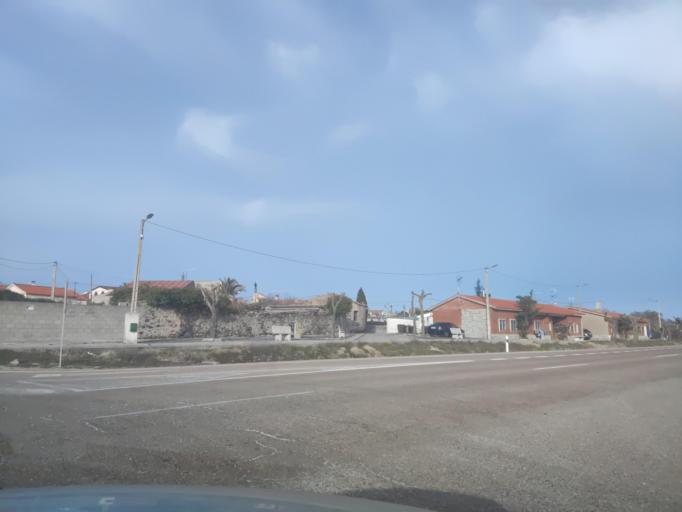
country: ES
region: Castille and Leon
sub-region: Provincia de Salamanca
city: Carpio de Azaba
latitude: 40.5947
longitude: -6.6475
